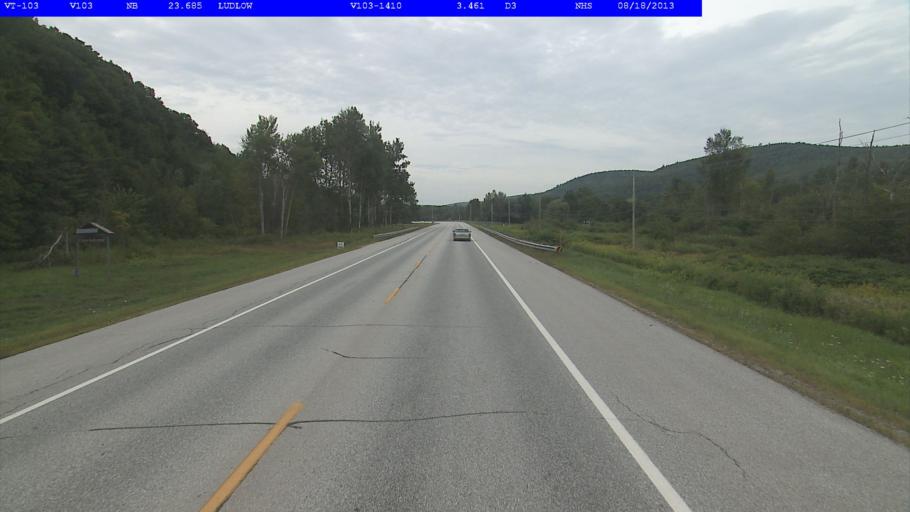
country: US
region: Vermont
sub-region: Windsor County
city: Chester
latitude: 43.4119
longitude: -72.7062
